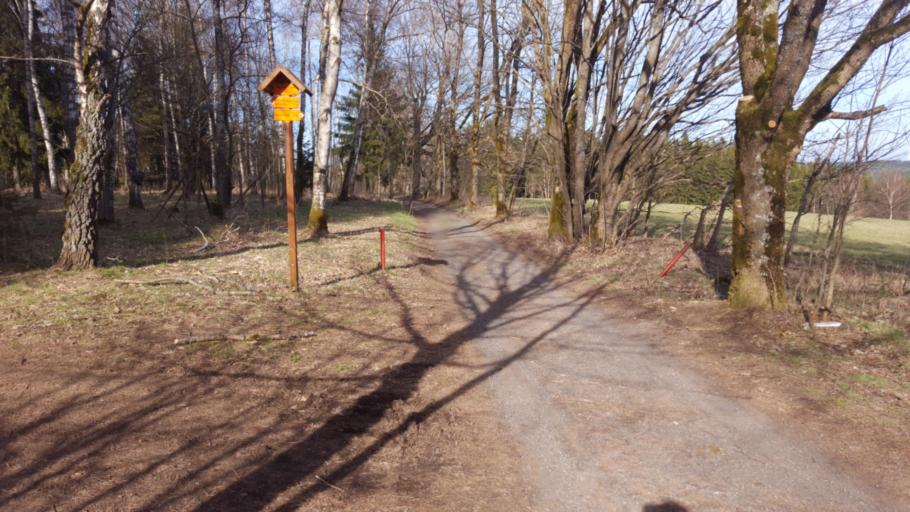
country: CZ
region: Karlovarsky
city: As
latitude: 50.2272
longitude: 12.2122
